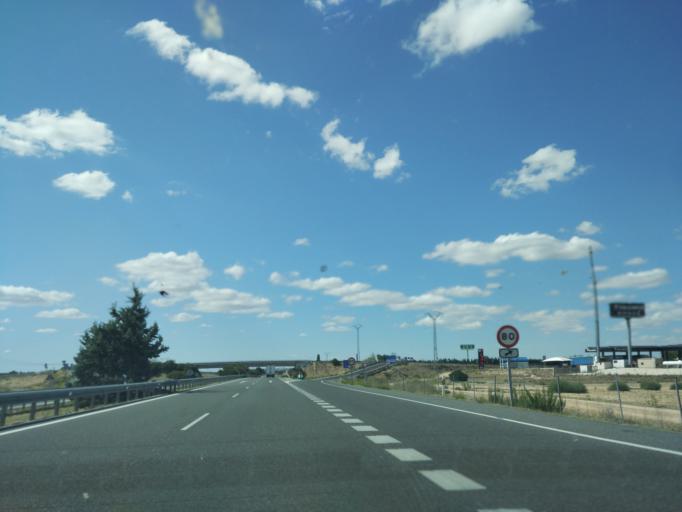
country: ES
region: Castille and Leon
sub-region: Provincia de Valladolid
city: San Vicente del Palacio
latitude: 41.2197
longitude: -4.8418
